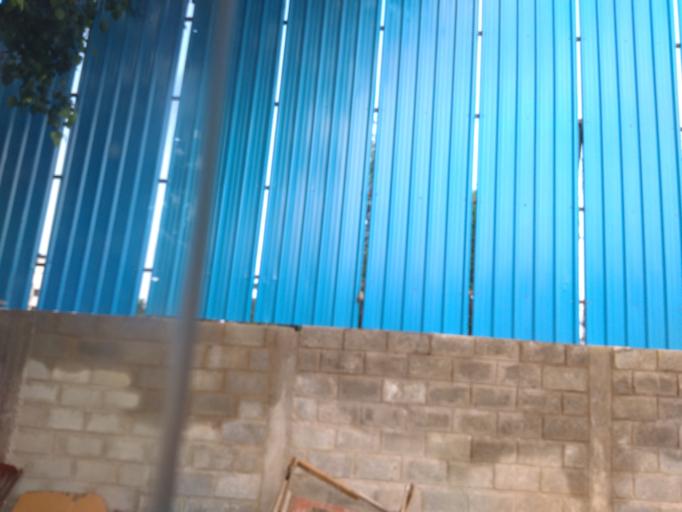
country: IN
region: Tamil Nadu
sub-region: Chennai
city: Gandhi Nagar
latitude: 12.9869
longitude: 80.2557
